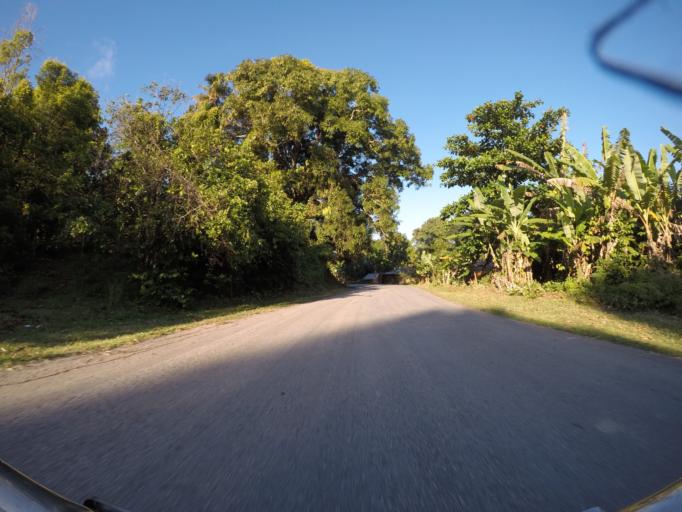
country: TZ
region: Pemba South
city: Mtambile
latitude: -5.3767
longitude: 39.6940
